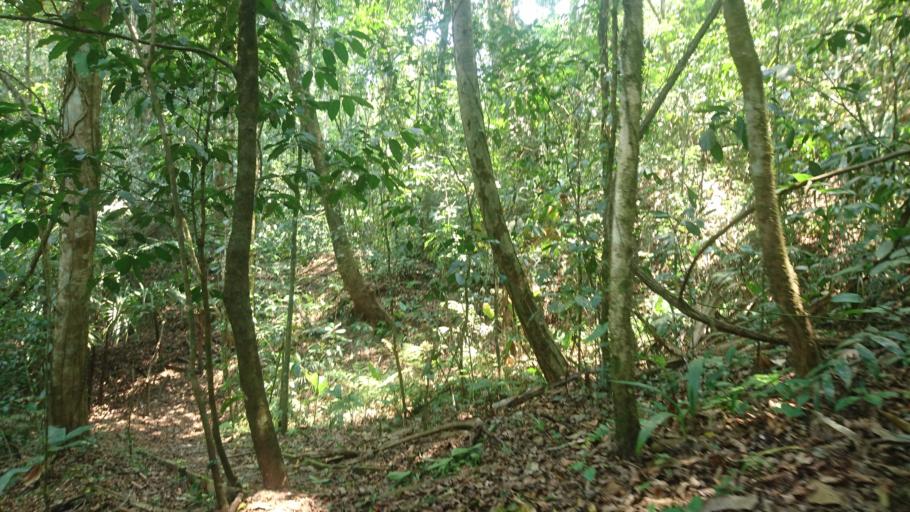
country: MX
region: Chiapas
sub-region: Marques de Comillas
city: Zamora Pico de Oro
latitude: 16.2478
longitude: -90.8342
